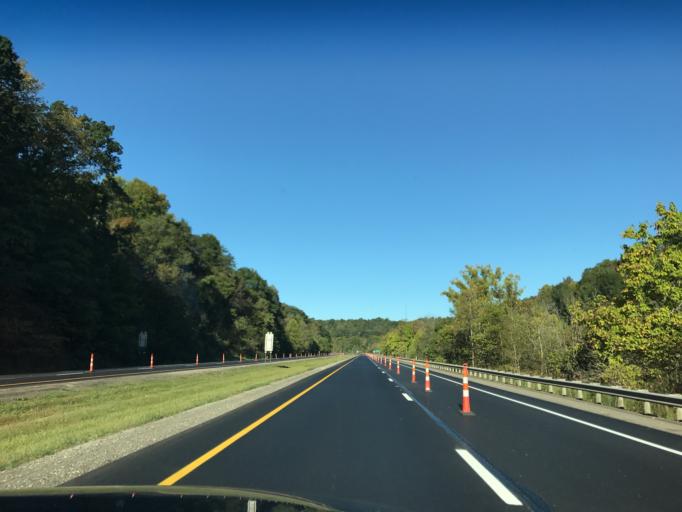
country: US
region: Ohio
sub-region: Washington County
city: Reno
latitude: 39.2455
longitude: -81.3742
